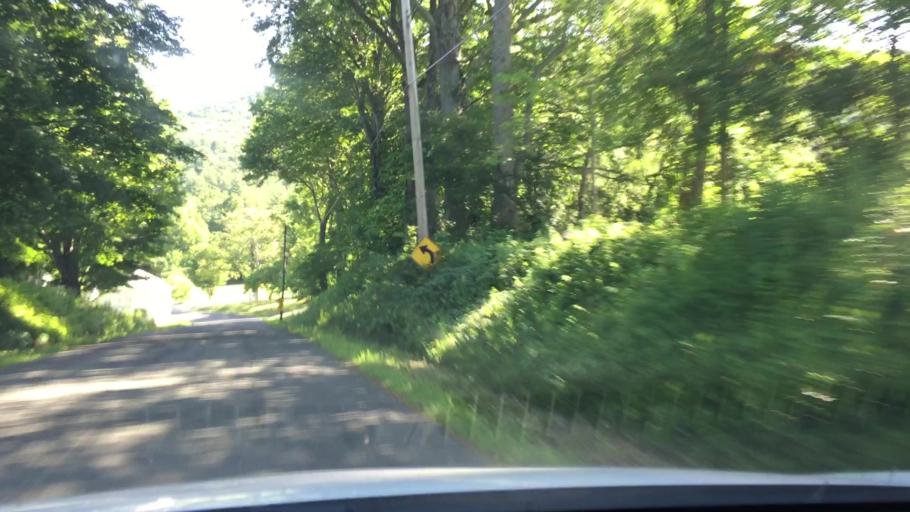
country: US
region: Massachusetts
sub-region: Berkshire County
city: Lee
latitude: 42.2434
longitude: -73.2052
